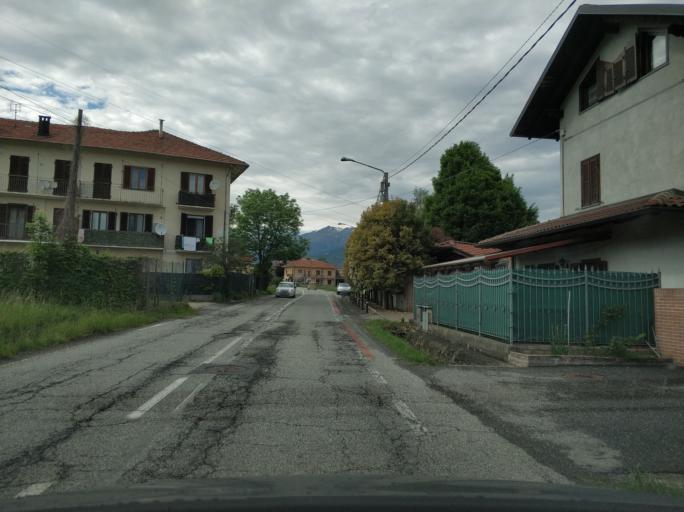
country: IT
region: Piedmont
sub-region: Provincia di Torino
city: Cafasse
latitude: 45.2388
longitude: 7.5229
